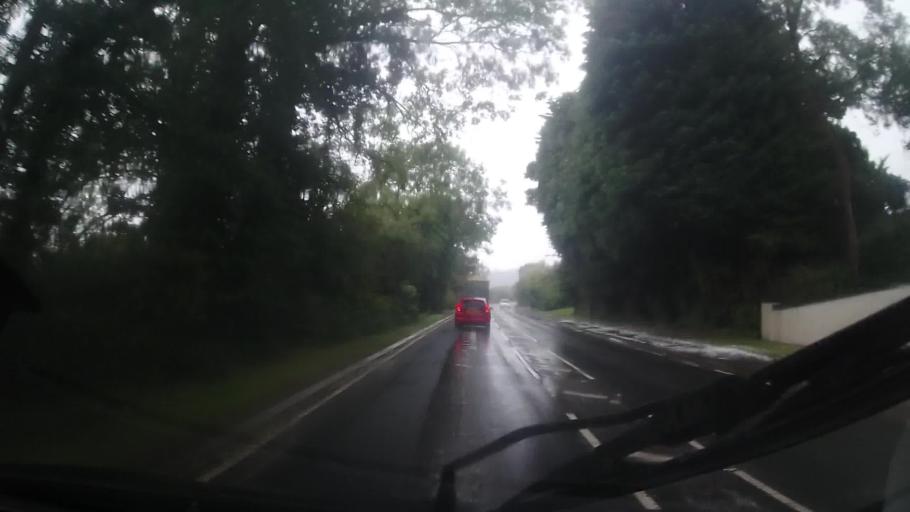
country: GB
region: England
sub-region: Worcestershire
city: Evesham
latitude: 52.1171
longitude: -1.9720
